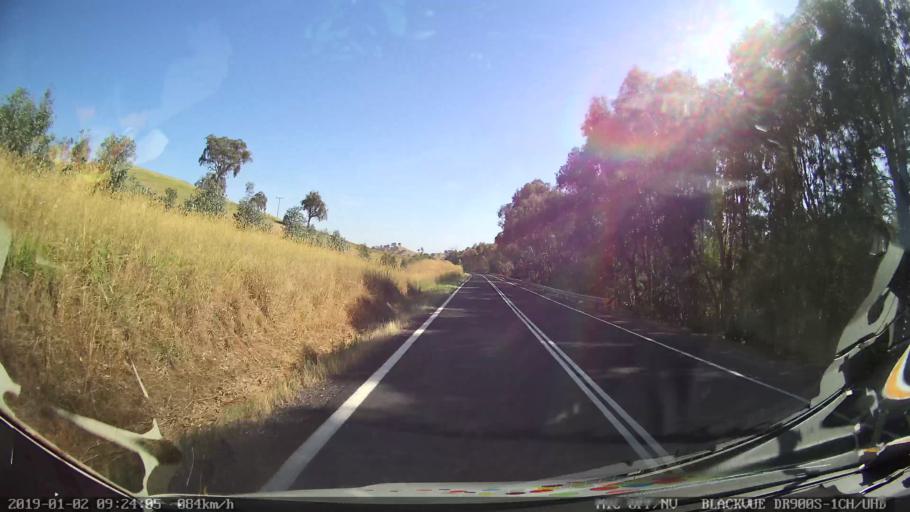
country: AU
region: New South Wales
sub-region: Tumut Shire
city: Tumut
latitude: -35.3817
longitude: 148.2915
